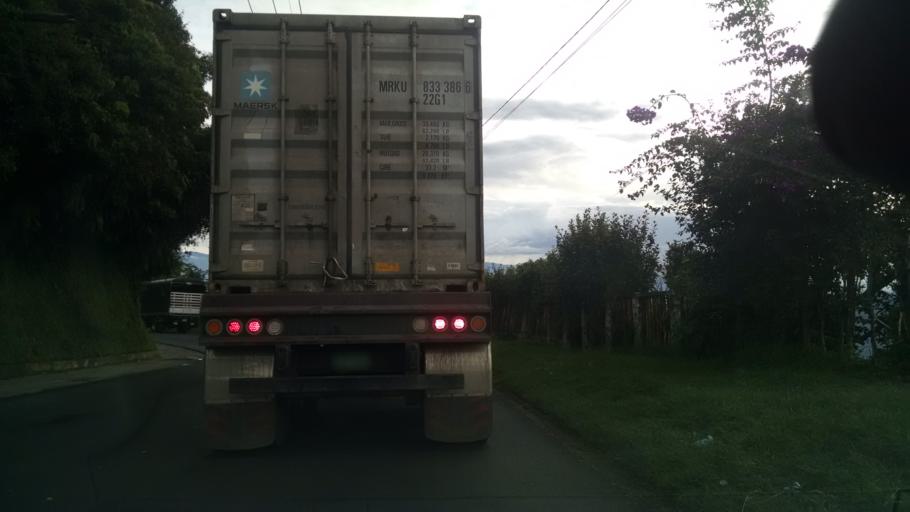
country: CO
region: Antioquia
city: Santa Barbara
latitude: 5.9209
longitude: -75.5787
